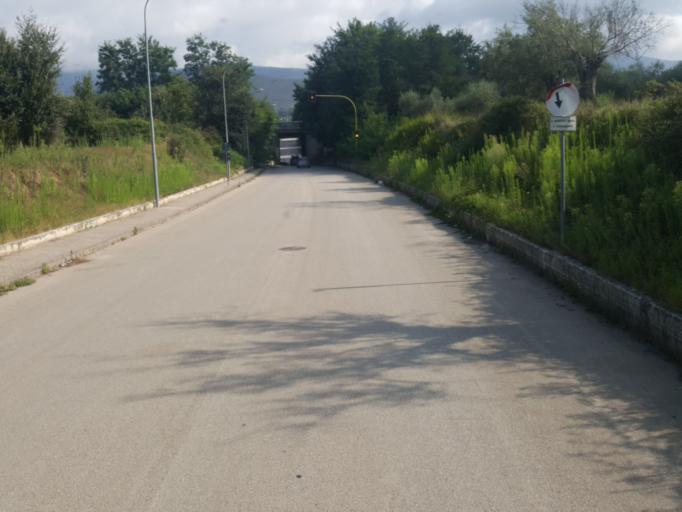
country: IT
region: Campania
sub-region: Provincia di Caserta
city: Pignataro Maggiore
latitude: 41.1831
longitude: 14.1590
